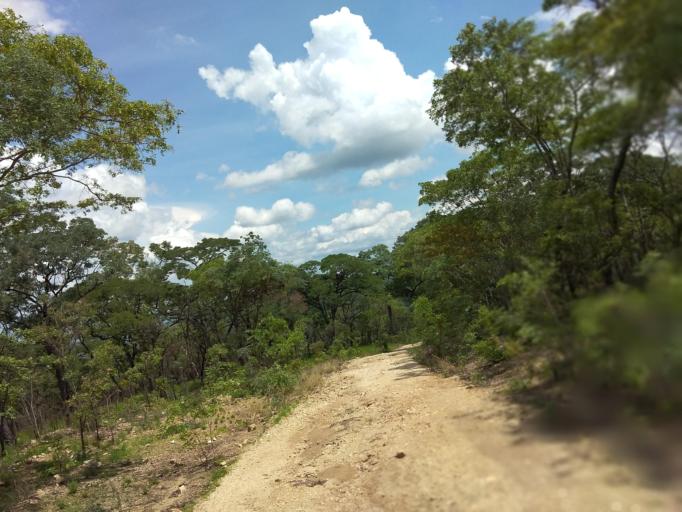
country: ZM
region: Central
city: Mkushi
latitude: -14.0790
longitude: 29.9698
